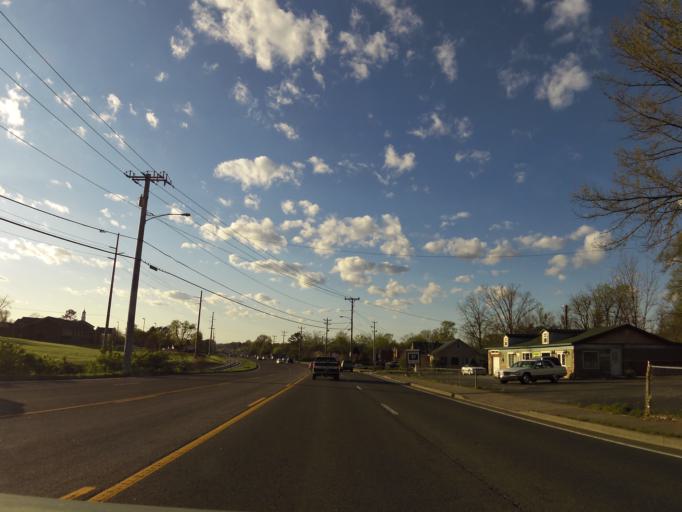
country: US
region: Tennessee
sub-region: Davidson County
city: Lakewood
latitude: 36.2365
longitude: -86.6275
